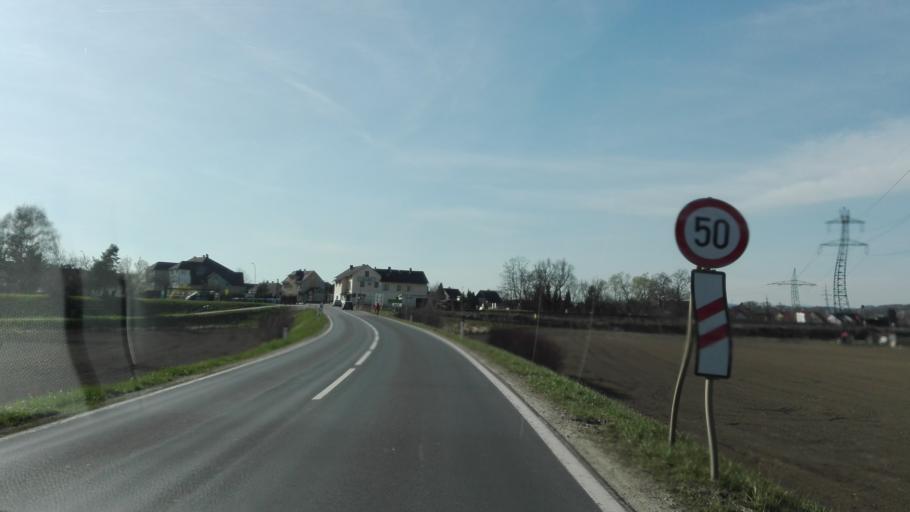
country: AT
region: Lower Austria
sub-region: Politischer Bezirk Amstetten
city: Ennsdorf
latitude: 48.2272
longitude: 14.5307
